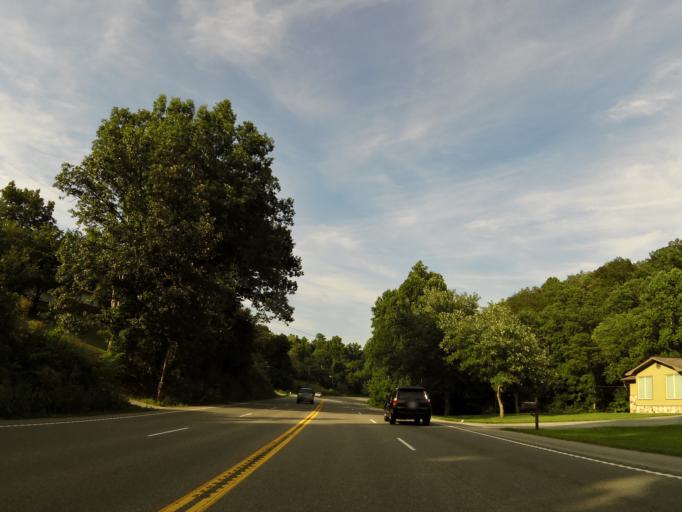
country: US
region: Tennessee
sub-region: Sevier County
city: Seymour
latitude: 35.8522
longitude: -83.6875
